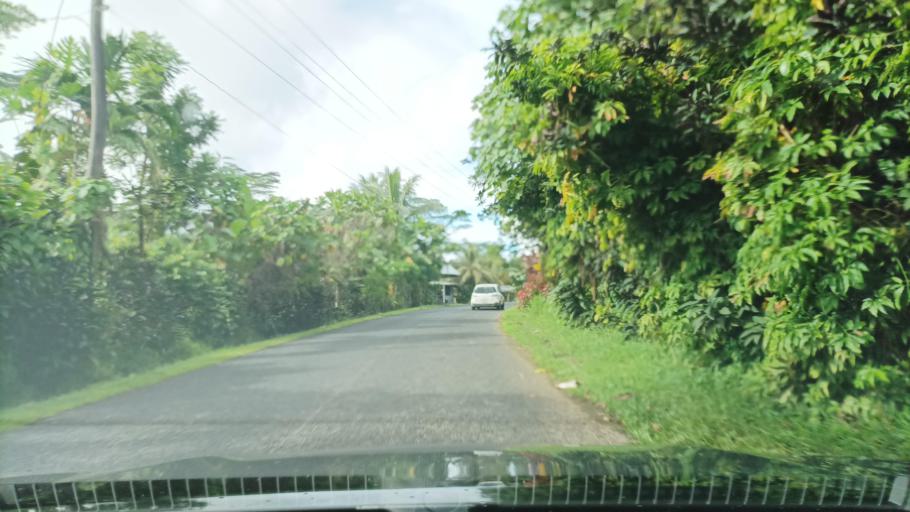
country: FM
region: Pohnpei
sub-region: Sokehs Municipality
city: Palikir - National Government Center
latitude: 6.9182
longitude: 158.1602
